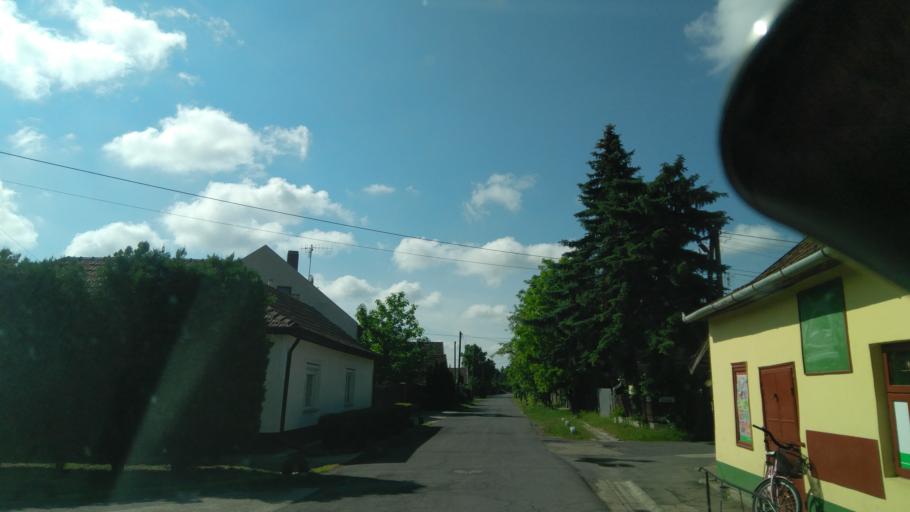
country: HU
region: Bekes
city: Bekes
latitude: 46.7822
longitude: 21.1238
